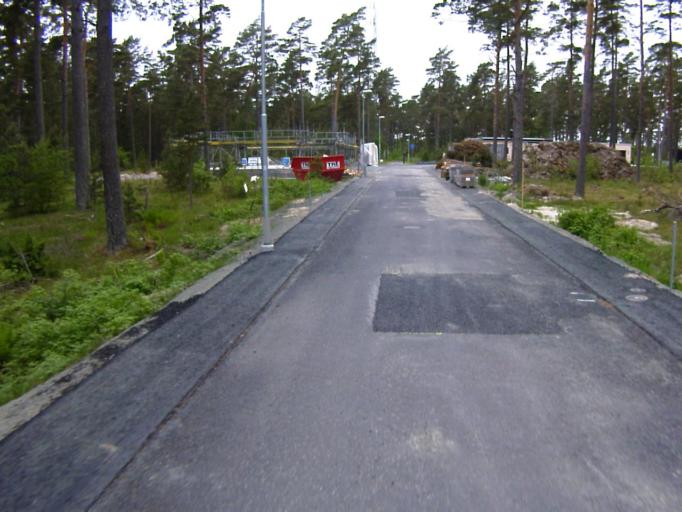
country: SE
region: Skane
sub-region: Kristianstads Kommun
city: Ahus
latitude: 55.9065
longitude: 14.2722
